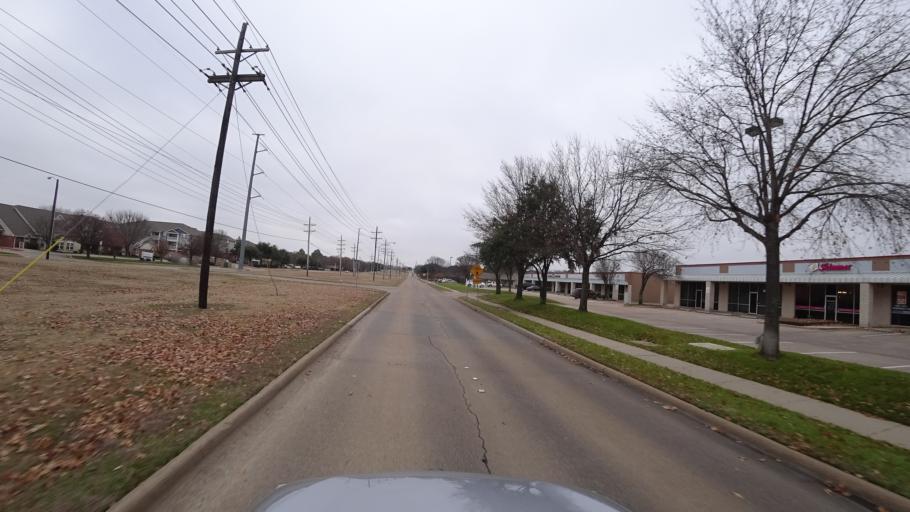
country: US
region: Texas
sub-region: Denton County
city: Highland Village
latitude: 33.0559
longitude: -97.0358
